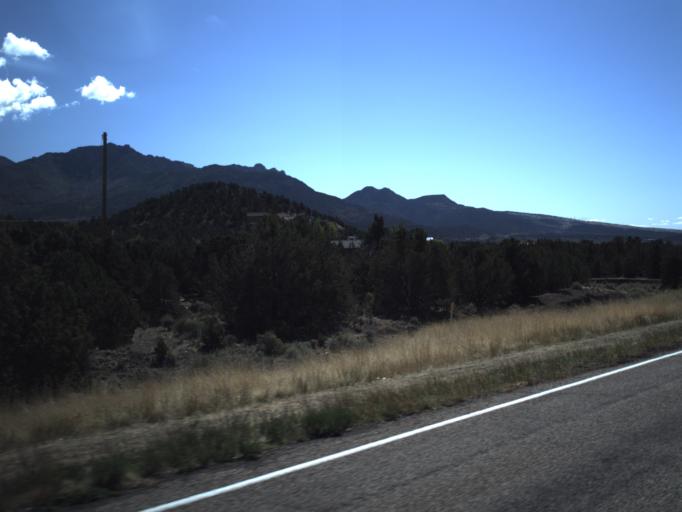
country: US
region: Utah
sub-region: Washington County
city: Enterprise
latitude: 37.4245
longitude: -113.6302
